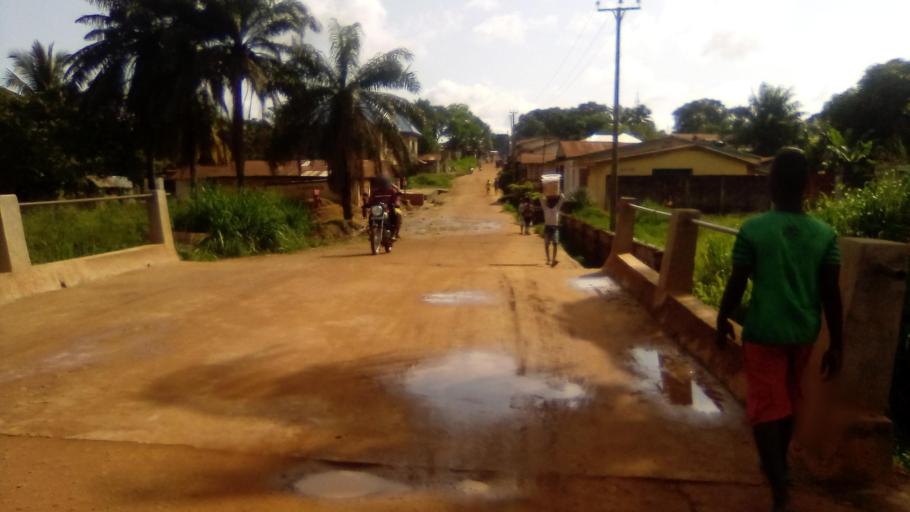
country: SL
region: Southern Province
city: Bo
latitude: 7.9758
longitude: -11.7292
